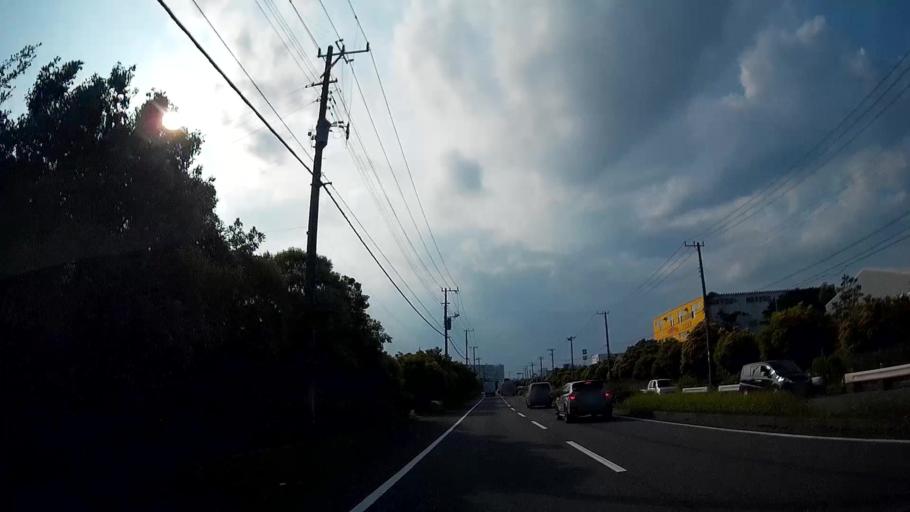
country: JP
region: Chiba
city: Funabashi
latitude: 35.6689
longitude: 140.0044
